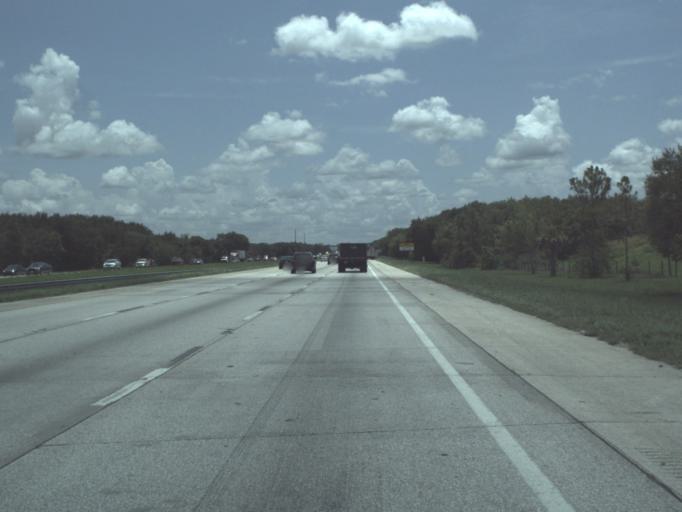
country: US
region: Florida
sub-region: Hillsborough County
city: Temple Terrace
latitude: 28.0278
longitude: -82.3410
